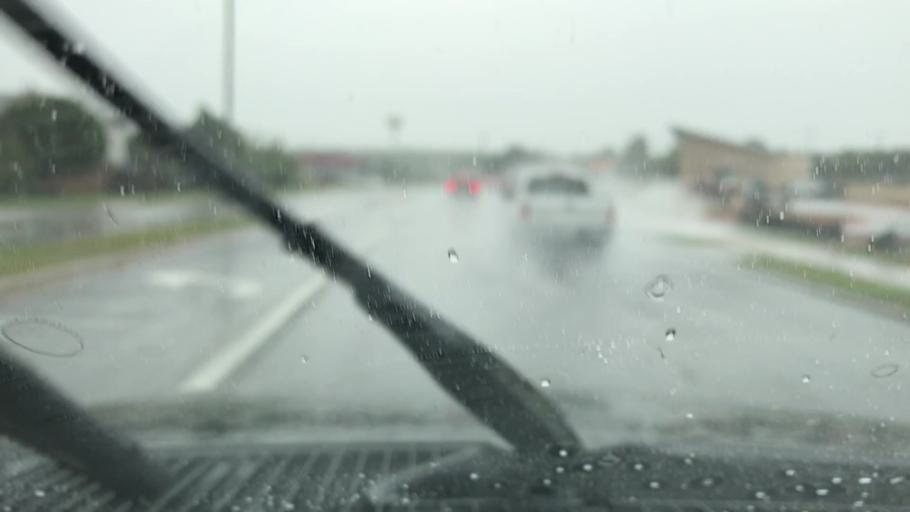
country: US
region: Texas
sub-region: Williamson County
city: Cedar Park
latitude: 30.5287
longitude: -97.8563
